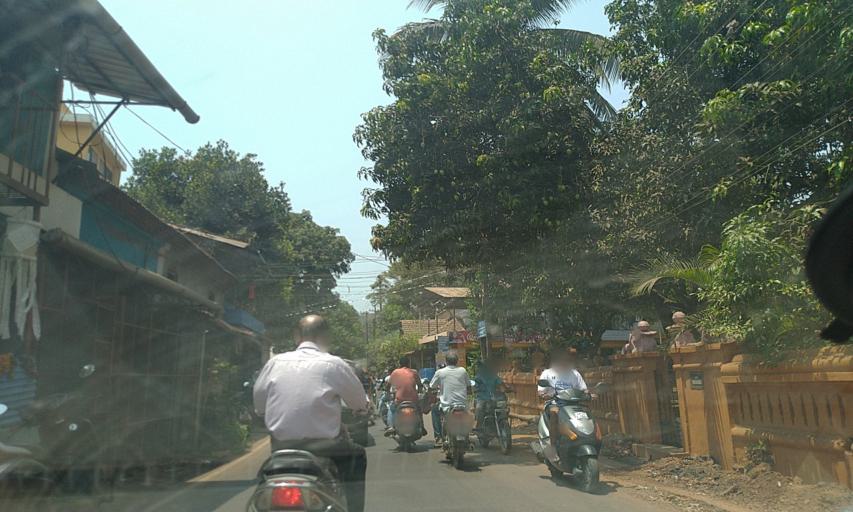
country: IN
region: Goa
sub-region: North Goa
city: Mapuca
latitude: 15.5937
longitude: 73.8037
